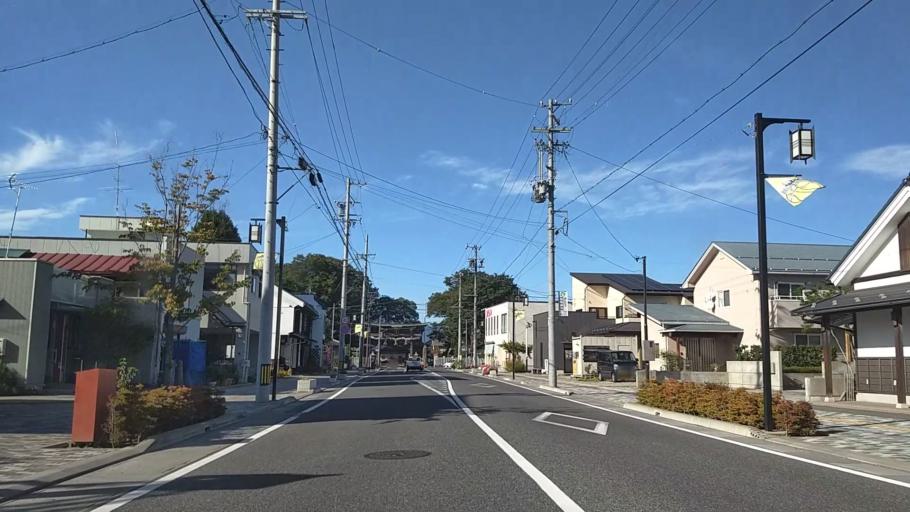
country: JP
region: Nagano
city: Nagano-shi
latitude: 36.5377
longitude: 138.1265
